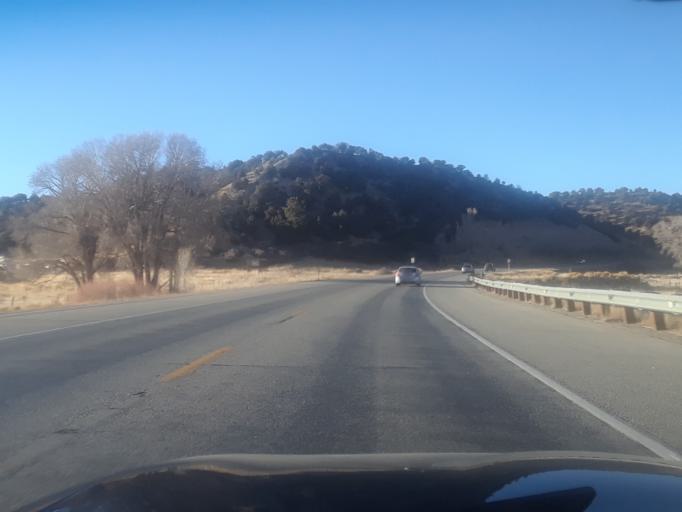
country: US
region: Colorado
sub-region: Chaffee County
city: Buena Vista
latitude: 38.7801
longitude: -106.1098
